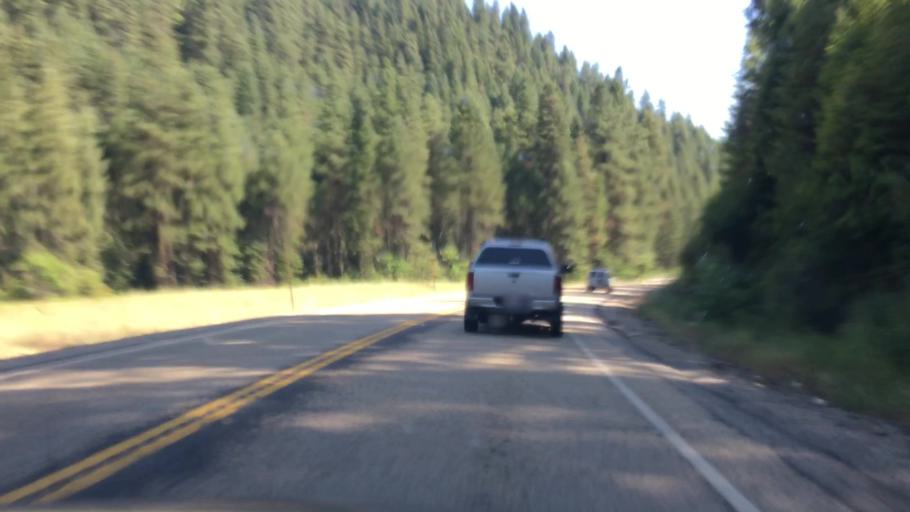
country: US
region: Idaho
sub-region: Valley County
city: Cascade
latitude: 44.1653
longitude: -116.1190
